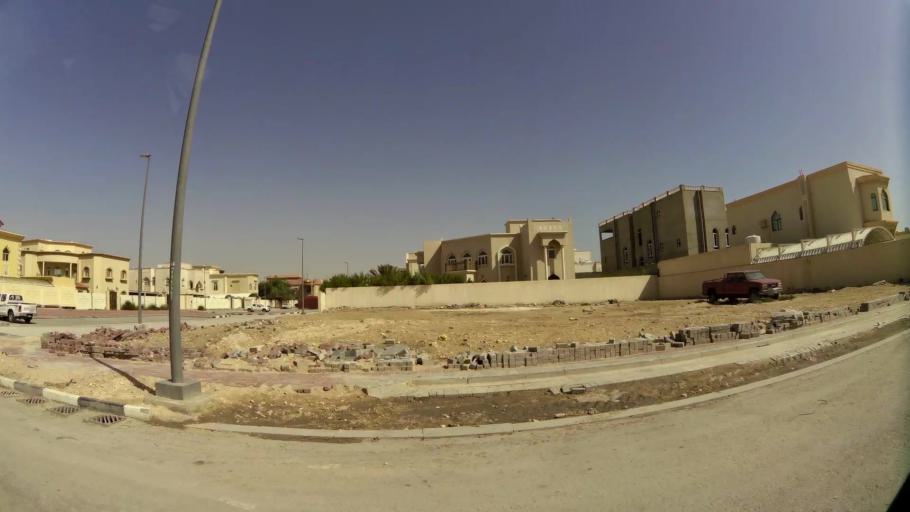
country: QA
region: Baladiyat ad Dawhah
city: Doha
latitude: 25.3605
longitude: 51.4983
